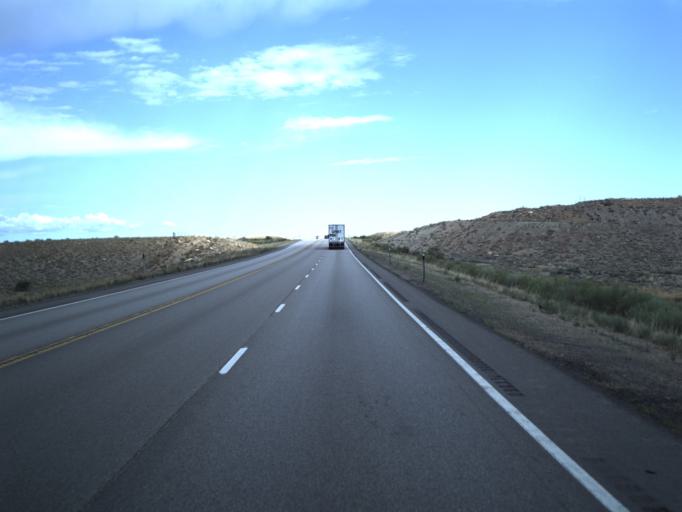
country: US
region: Utah
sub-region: Carbon County
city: East Carbon City
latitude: 39.4986
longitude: -110.5256
